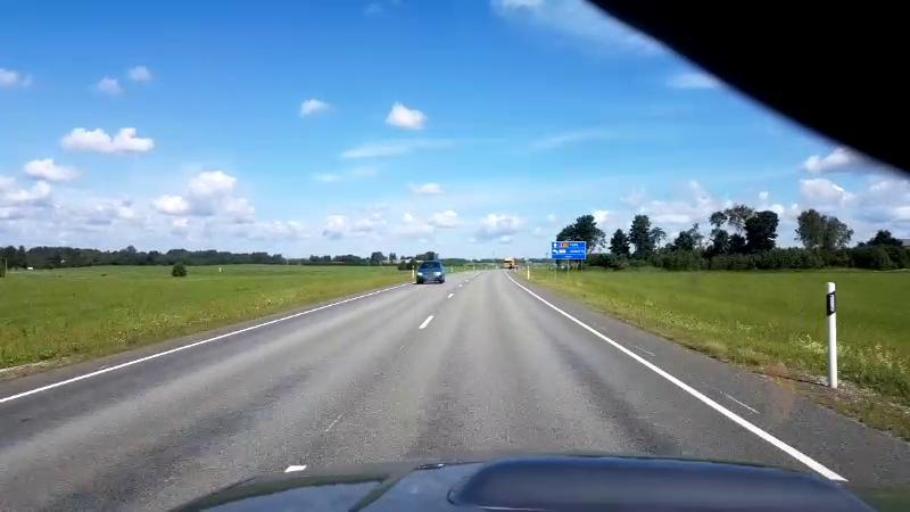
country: EE
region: Jaervamaa
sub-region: Jaerva-Jaani vald
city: Jarva-Jaani
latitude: 59.1678
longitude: 25.7582
